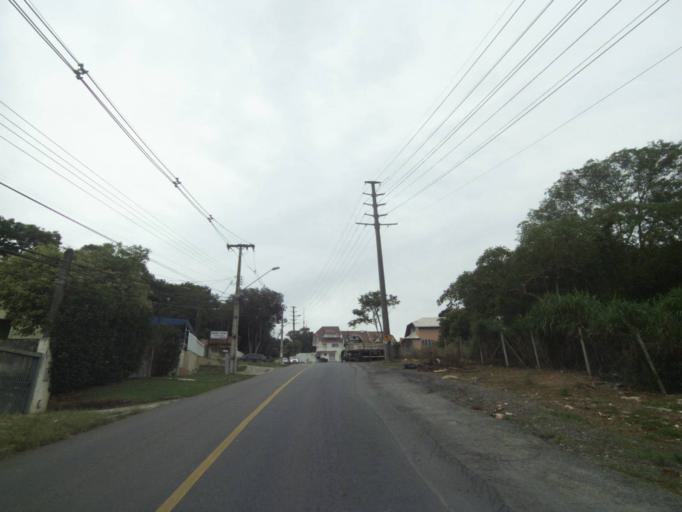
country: BR
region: Parana
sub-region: Curitiba
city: Curitiba
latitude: -25.3969
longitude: -49.2809
